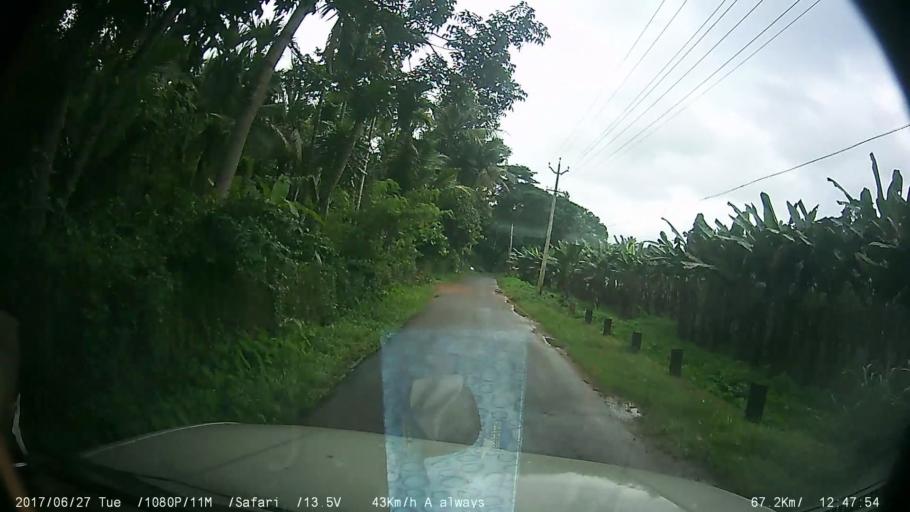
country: IN
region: Kerala
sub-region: Ernakulam
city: Piravam
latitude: 9.7779
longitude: 76.5187
